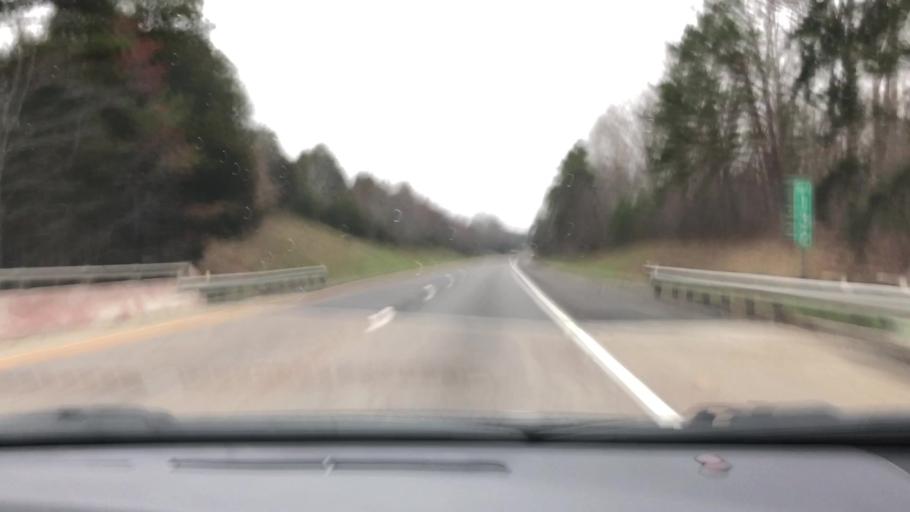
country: US
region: Virginia
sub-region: Fluvanna County
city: Lake Monticello
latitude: 37.9968
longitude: -78.2987
